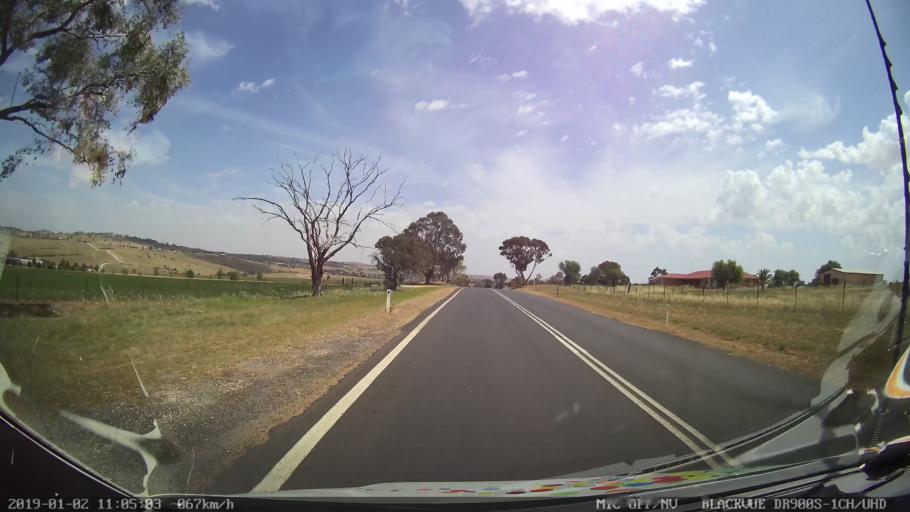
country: AU
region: New South Wales
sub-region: Young
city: Young
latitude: -34.5694
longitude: 148.3541
